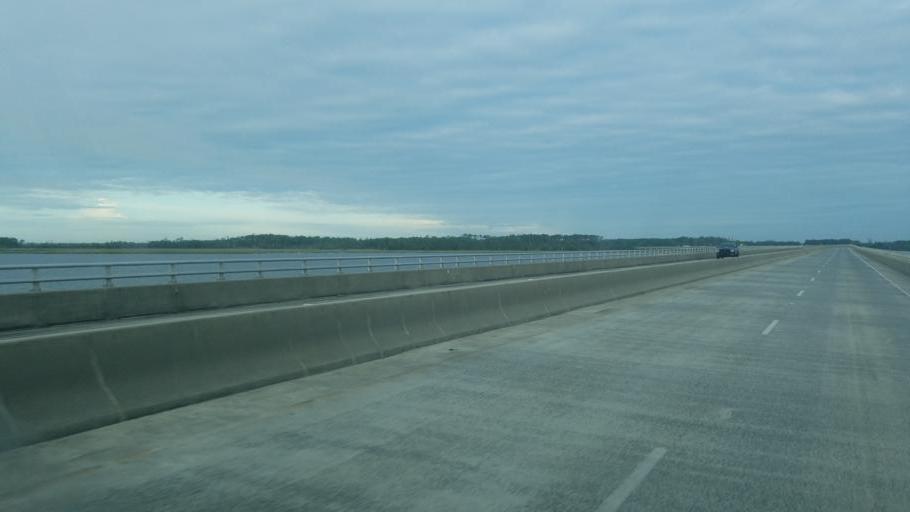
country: US
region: North Carolina
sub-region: Dare County
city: Manteo
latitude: 35.8882
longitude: -75.7437
